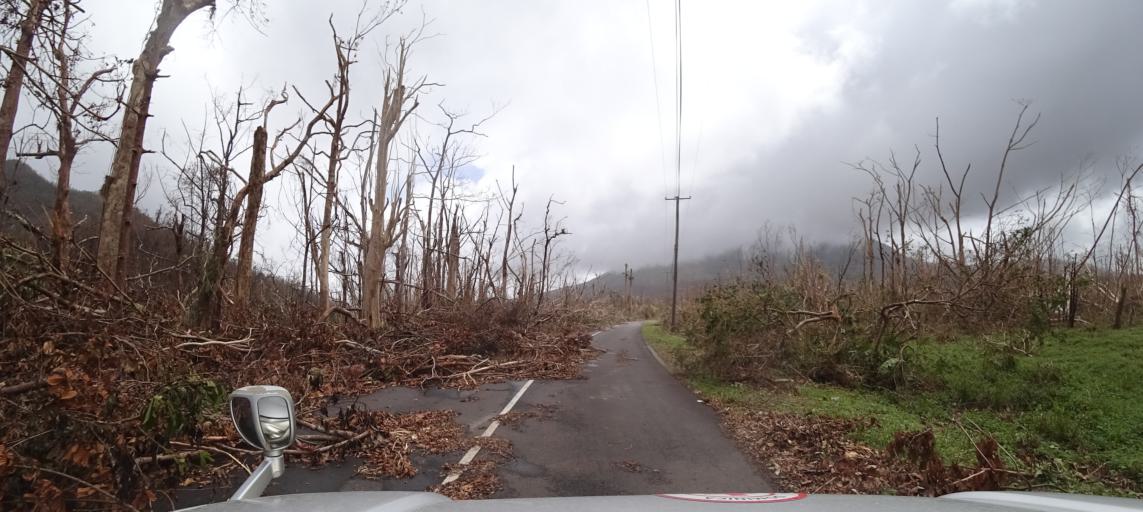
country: DM
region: Saint Paul
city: Pont Casse
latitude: 15.4054
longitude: -61.3426
